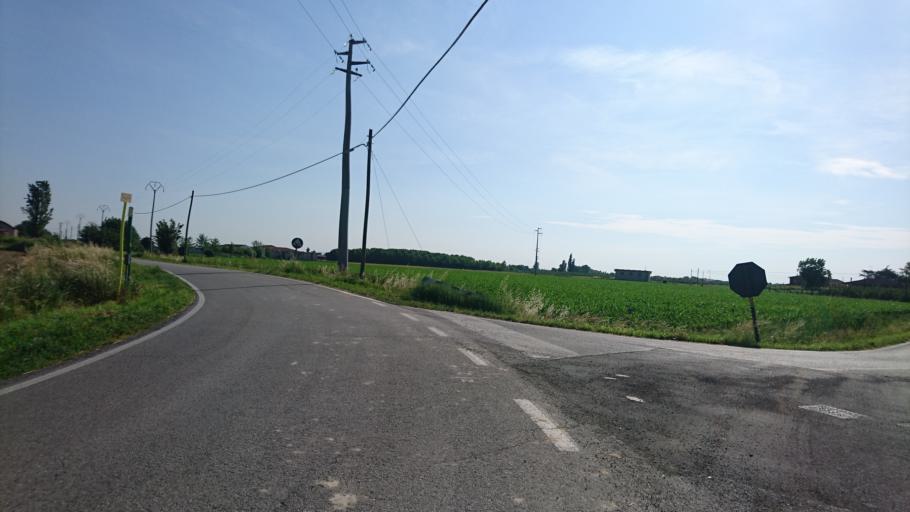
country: IT
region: Veneto
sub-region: Provincia di Verona
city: Terrazzo
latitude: 45.1700
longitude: 11.3809
